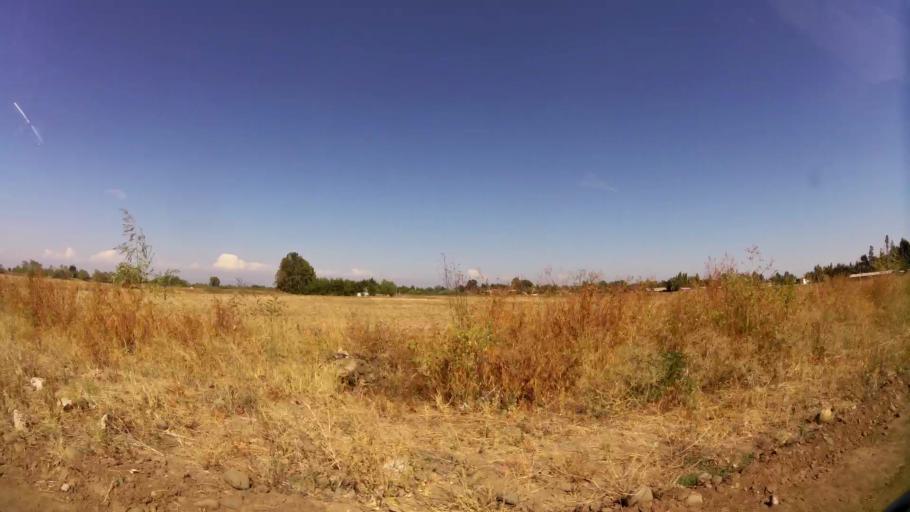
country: CL
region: Maule
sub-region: Provincia de Talca
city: Talca
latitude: -35.4169
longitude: -71.6020
